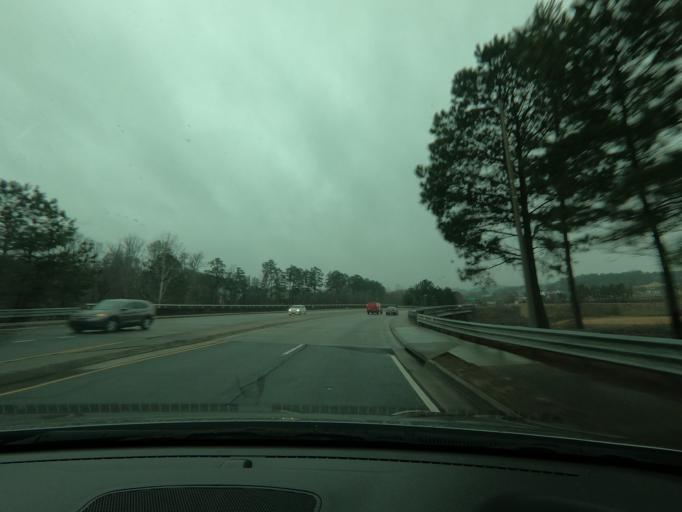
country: US
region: Georgia
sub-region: Cobb County
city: Kennesaw
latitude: 34.0223
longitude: -84.5522
